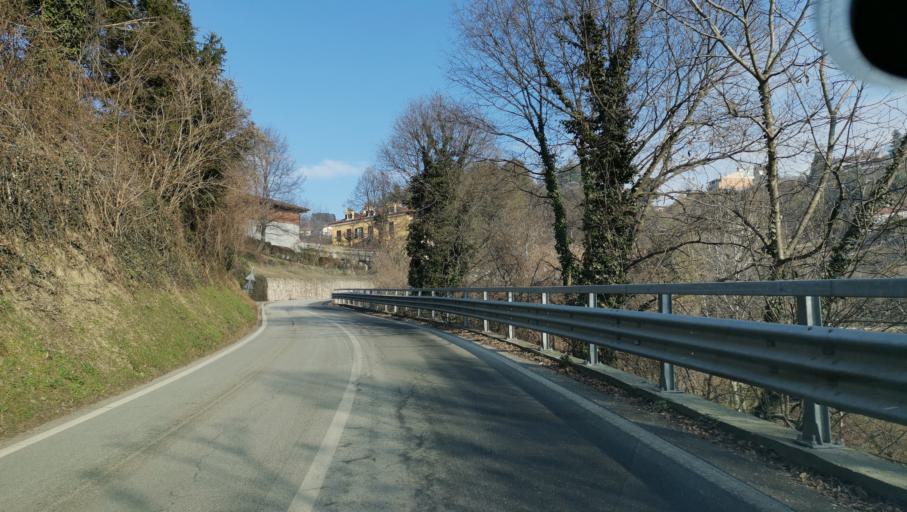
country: IT
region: Piedmont
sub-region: Provincia di Torino
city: Piana San Raffaele
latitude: 45.1495
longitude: 7.8603
